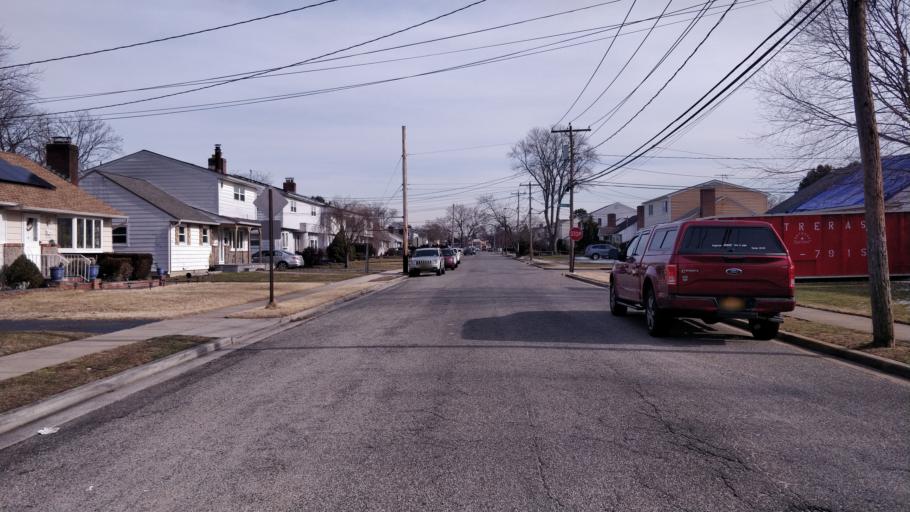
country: US
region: New York
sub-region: Nassau County
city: Hicksville
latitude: 40.7762
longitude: -73.5347
